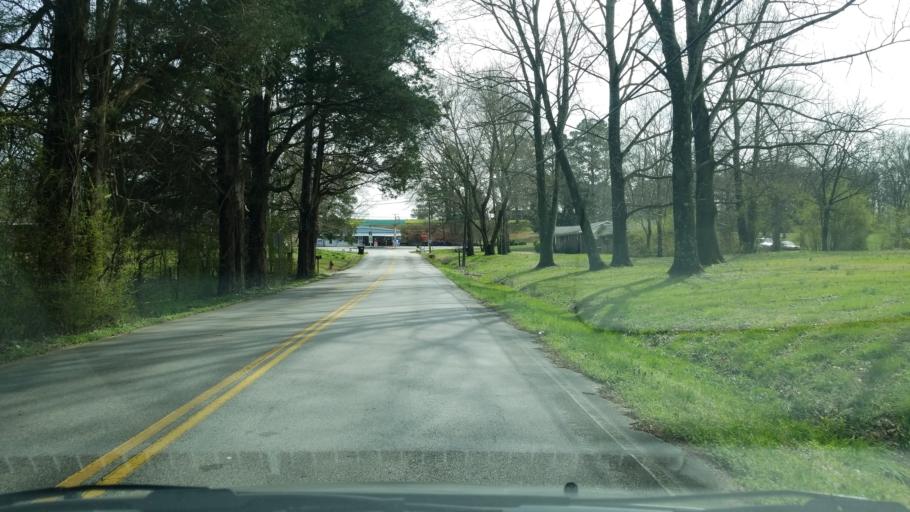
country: US
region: Tennessee
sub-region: Hamilton County
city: Harrison
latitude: 35.1331
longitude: -85.0716
